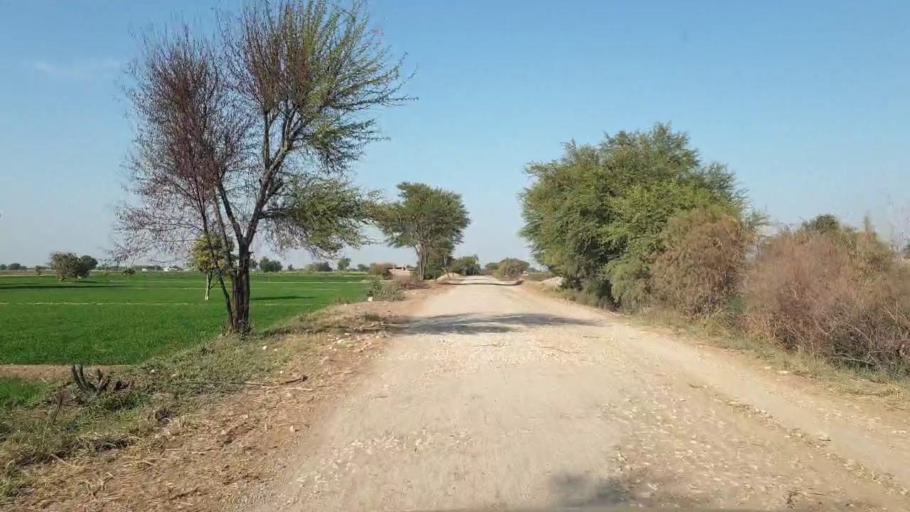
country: PK
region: Sindh
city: Shahpur Chakar
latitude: 26.1578
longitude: 68.6841
